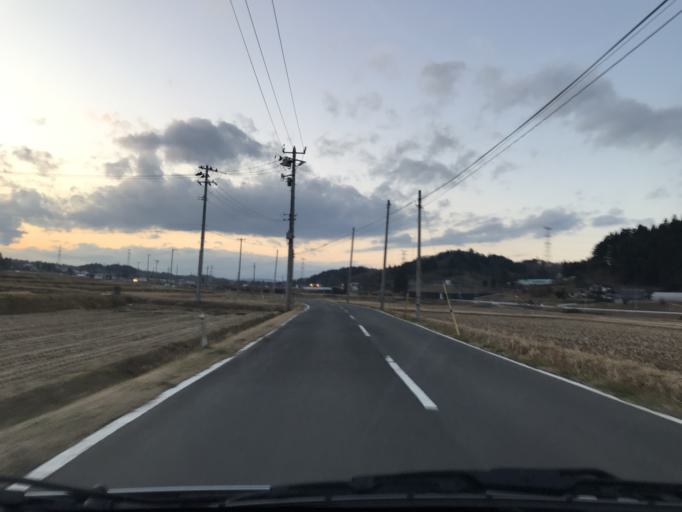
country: JP
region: Iwate
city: Ichinoseki
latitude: 38.8489
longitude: 141.1023
